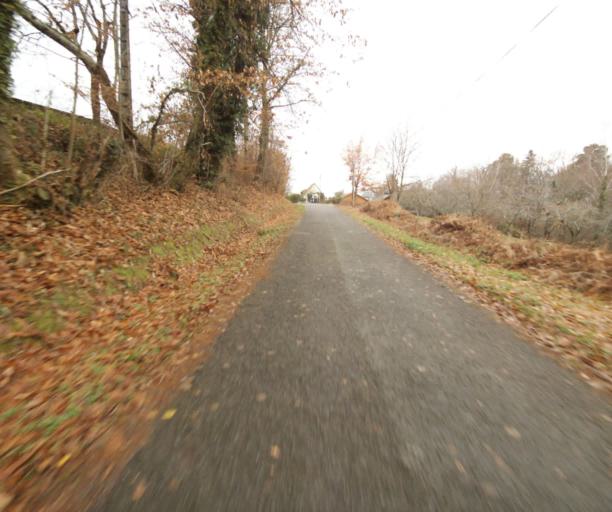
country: FR
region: Limousin
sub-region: Departement de la Correze
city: Tulle
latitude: 45.2653
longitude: 1.7327
